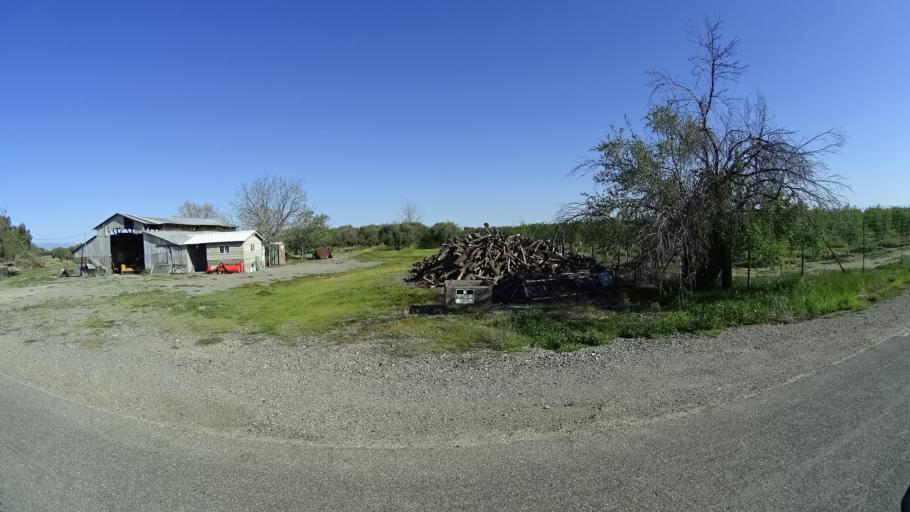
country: US
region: California
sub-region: Glenn County
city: Orland
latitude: 39.7476
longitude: -122.2252
